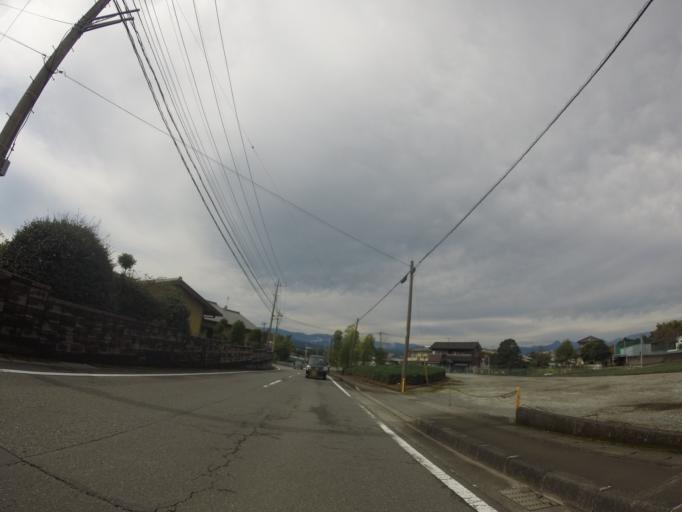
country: JP
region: Shizuoka
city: Fuji
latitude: 35.2053
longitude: 138.6626
